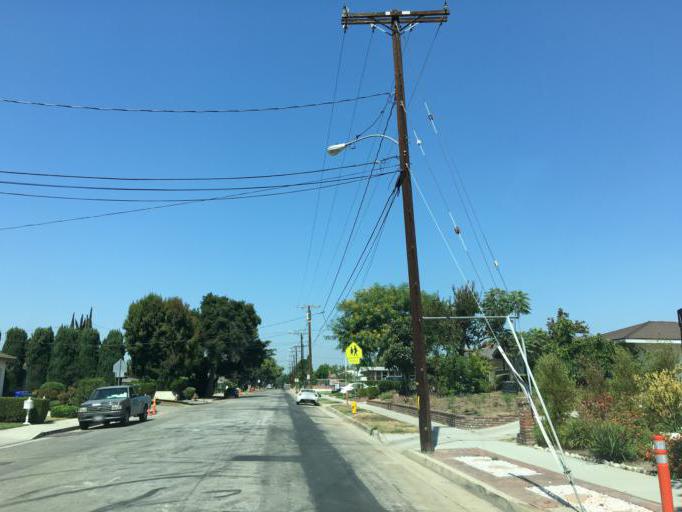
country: US
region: California
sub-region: Los Angeles County
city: San Marino
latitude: 34.1171
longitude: -118.0872
